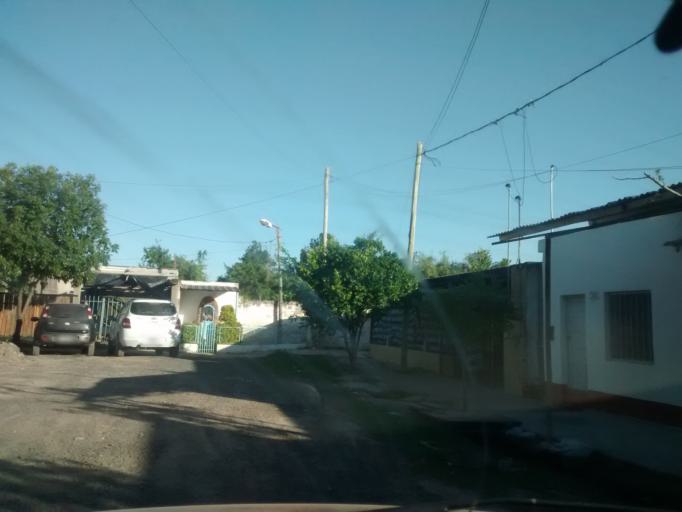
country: AR
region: Chaco
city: Resistencia
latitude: -27.4540
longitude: -59.0063
